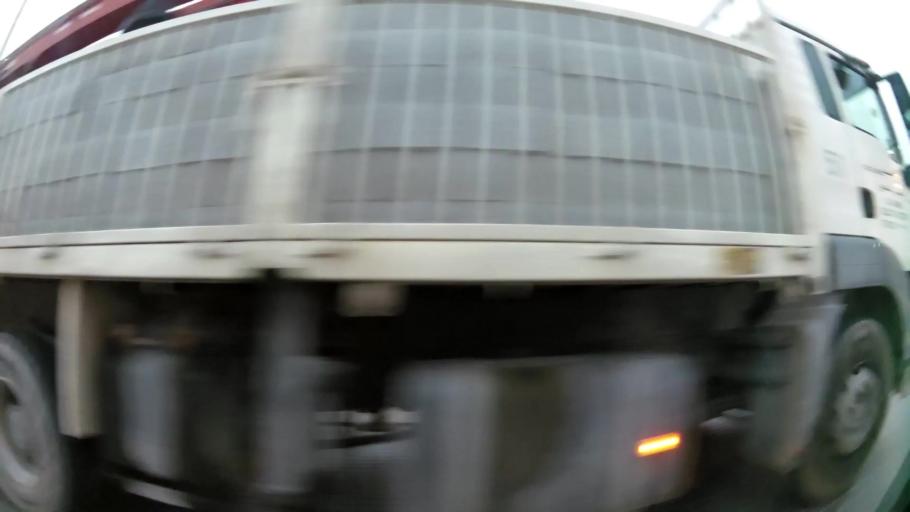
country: BH
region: Northern
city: Ar Rifa'
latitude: 26.1511
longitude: 50.5742
